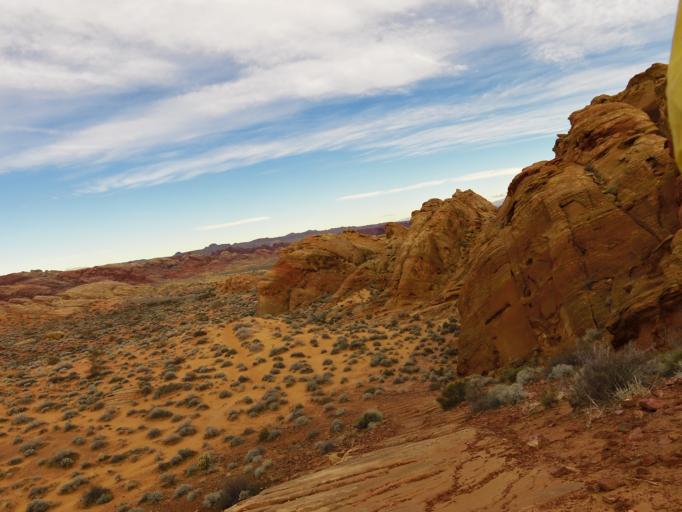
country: US
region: Nevada
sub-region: Clark County
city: Moapa Valley
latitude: 36.4502
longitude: -114.5116
